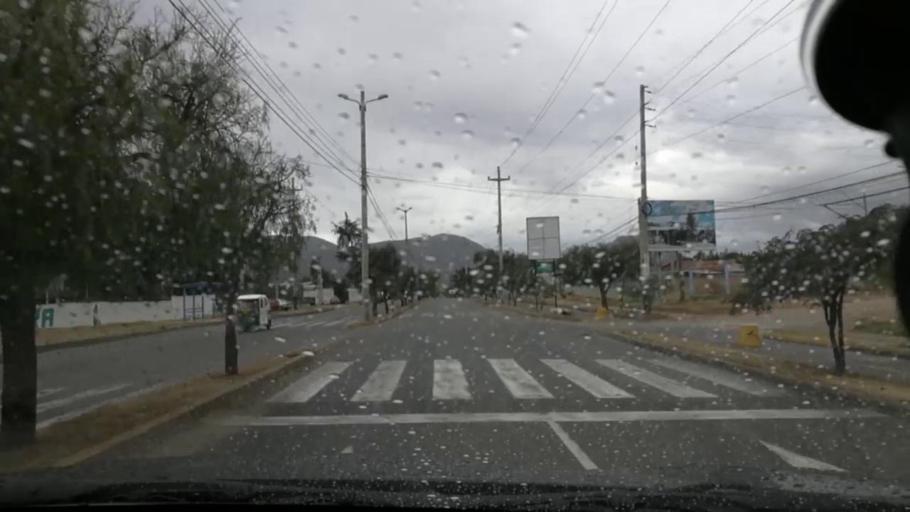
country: PE
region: Cajamarca
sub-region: Provincia de Cajamarca
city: Cajamarca
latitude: -7.1654
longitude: -78.4934
